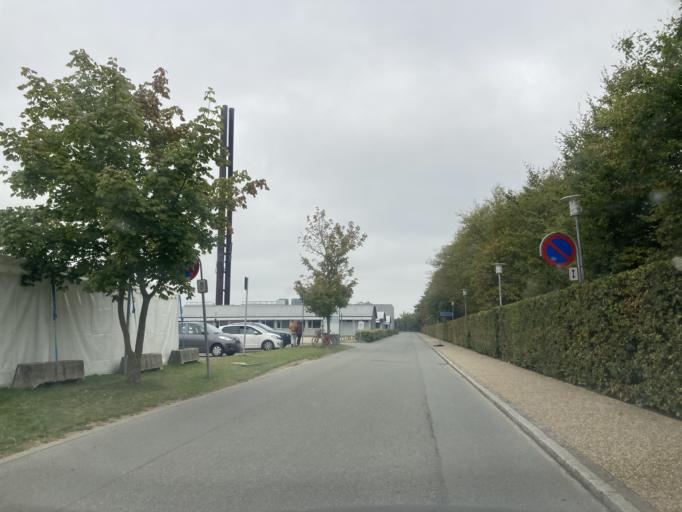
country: DK
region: Capital Region
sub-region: Hvidovre Kommune
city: Hvidovre
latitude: 55.6486
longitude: 12.4720
